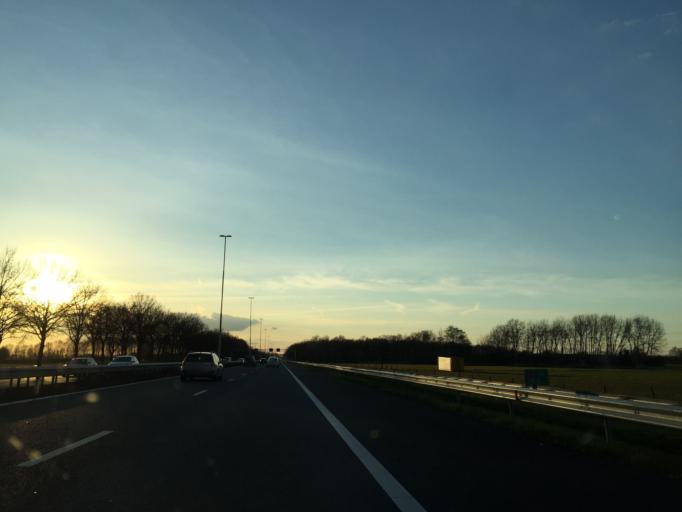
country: NL
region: North Brabant
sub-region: Gemeente Oirschot
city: Middelbeers
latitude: 51.5239
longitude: 5.2216
